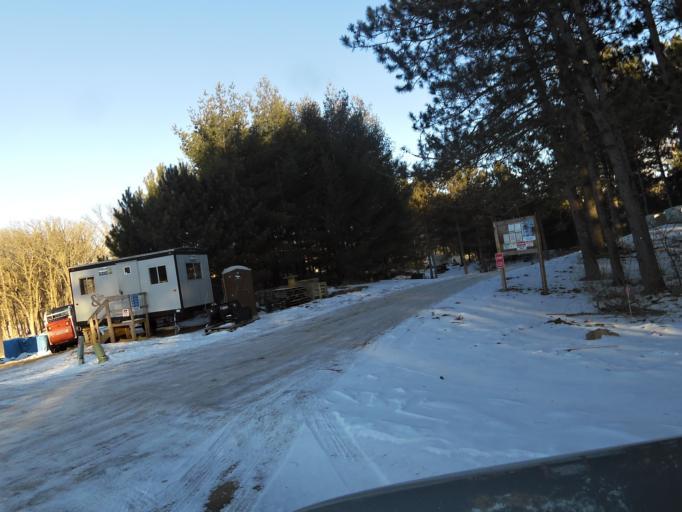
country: US
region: Minnesota
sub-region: Washington County
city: Lake Elmo
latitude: 44.9820
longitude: -92.8351
